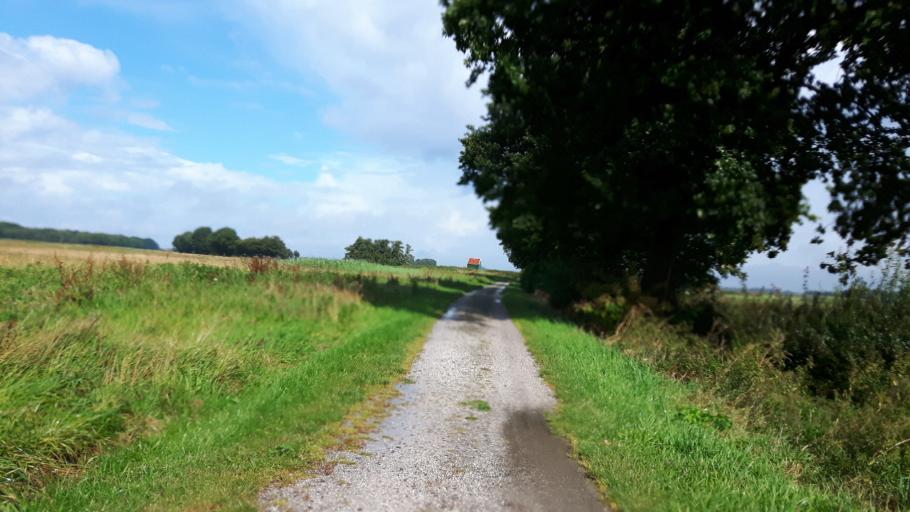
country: NL
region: Flevoland
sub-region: Gemeente Noordoostpolder
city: Ens
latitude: 52.6258
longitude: 5.7763
